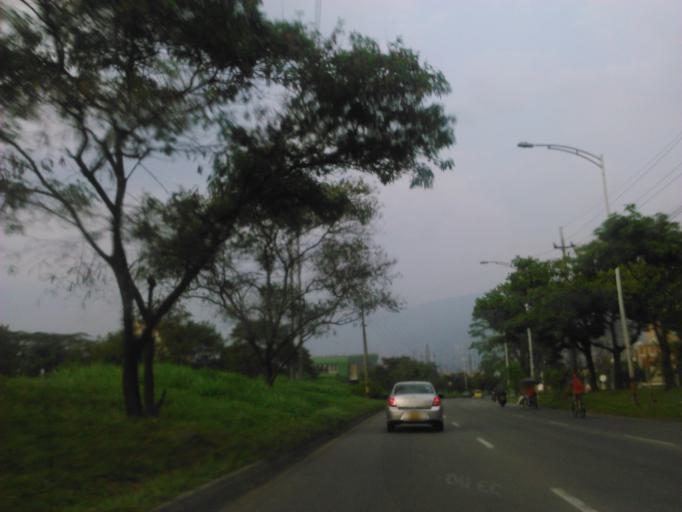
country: CO
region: Antioquia
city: Sabaneta
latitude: 6.1612
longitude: -75.6097
